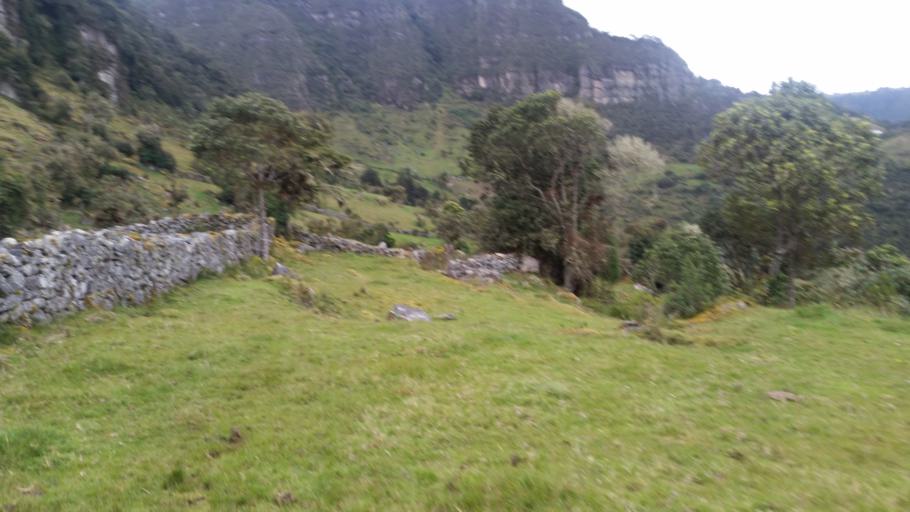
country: CO
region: Cundinamarca
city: Choachi
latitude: 4.5542
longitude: -73.9696
